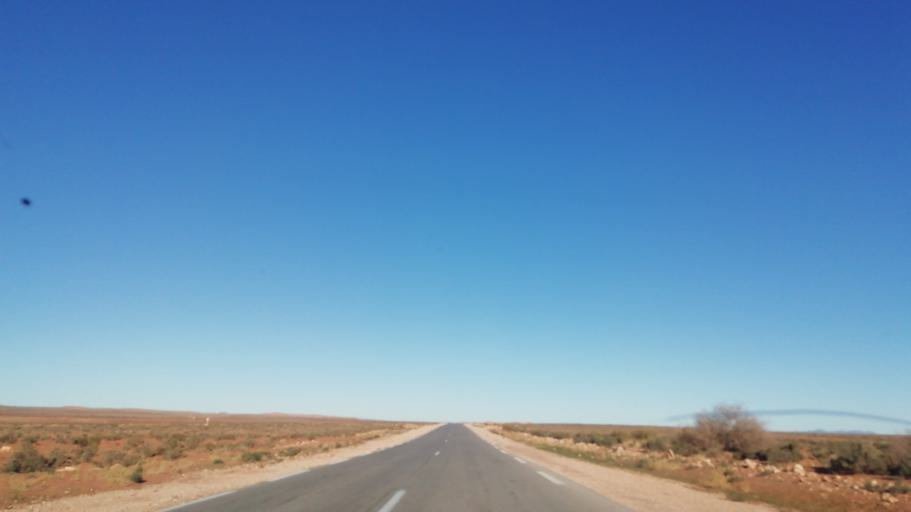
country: DZ
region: El Bayadh
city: El Abiodh Sidi Cheikh
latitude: 33.1170
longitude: 0.2684
